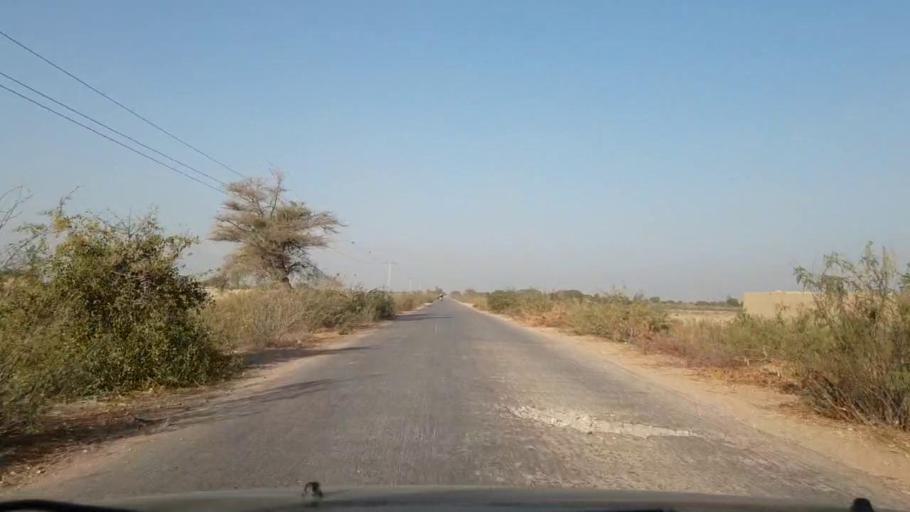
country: PK
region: Sindh
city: Chambar
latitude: 25.2531
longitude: 68.7932
